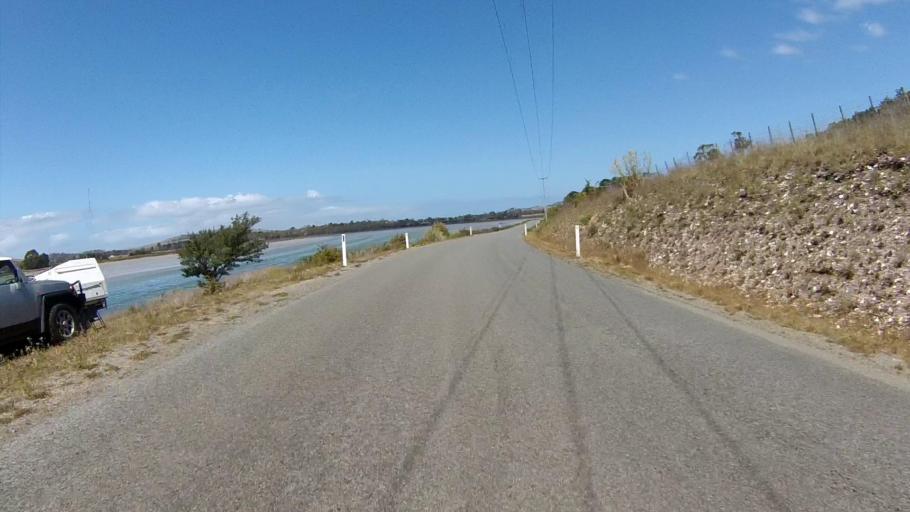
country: AU
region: Tasmania
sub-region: Clarence
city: Lauderdale
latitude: -42.9199
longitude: 147.4789
